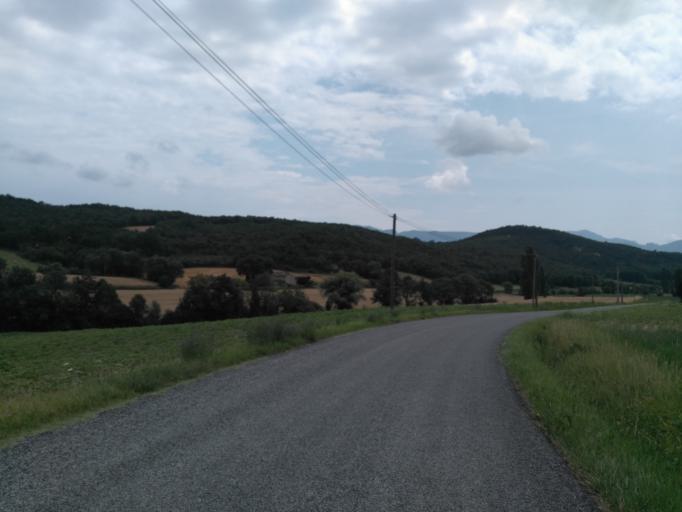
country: FR
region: Rhone-Alpes
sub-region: Departement de la Drome
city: Aouste-sur-Sye
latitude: 44.7557
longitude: 5.1171
